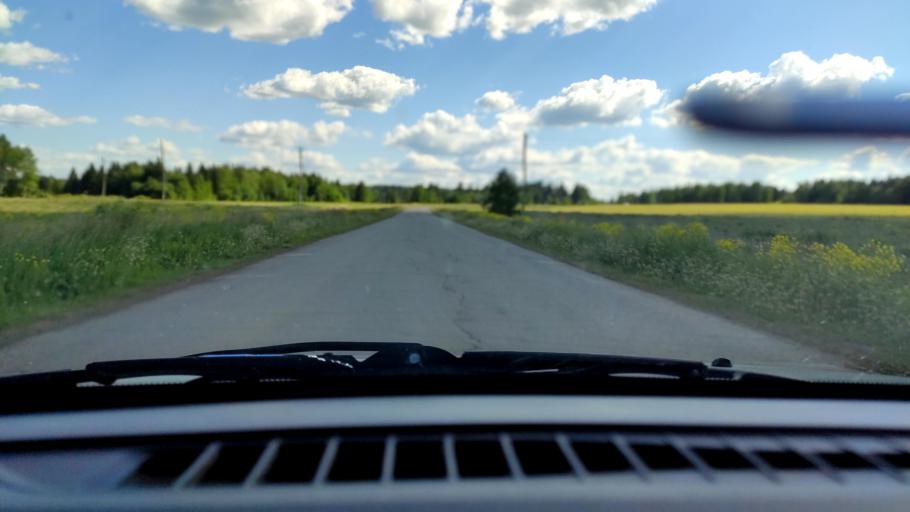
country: RU
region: Perm
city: Uinskoye
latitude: 57.1462
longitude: 56.5702
